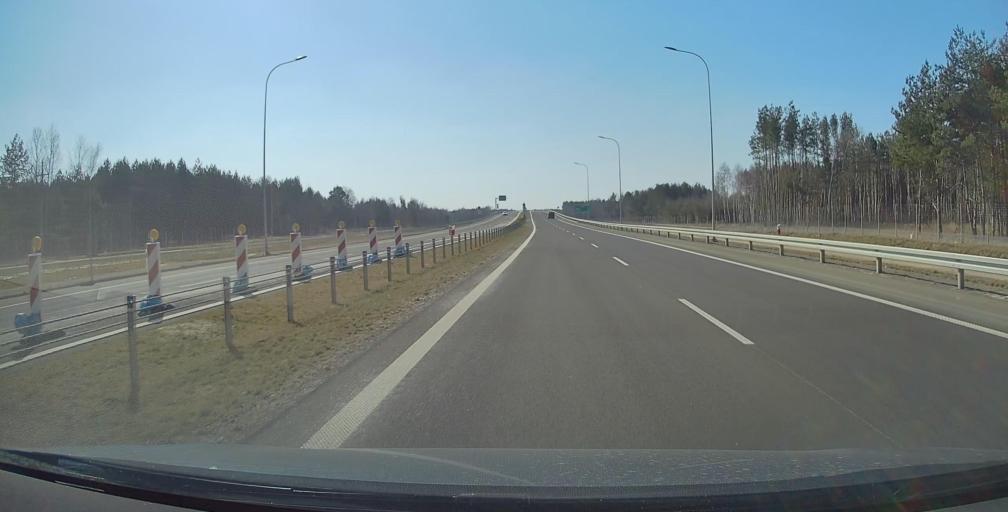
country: PL
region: Subcarpathian Voivodeship
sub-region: Powiat nizanski
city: Przedzel
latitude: 50.4905
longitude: 22.1923
